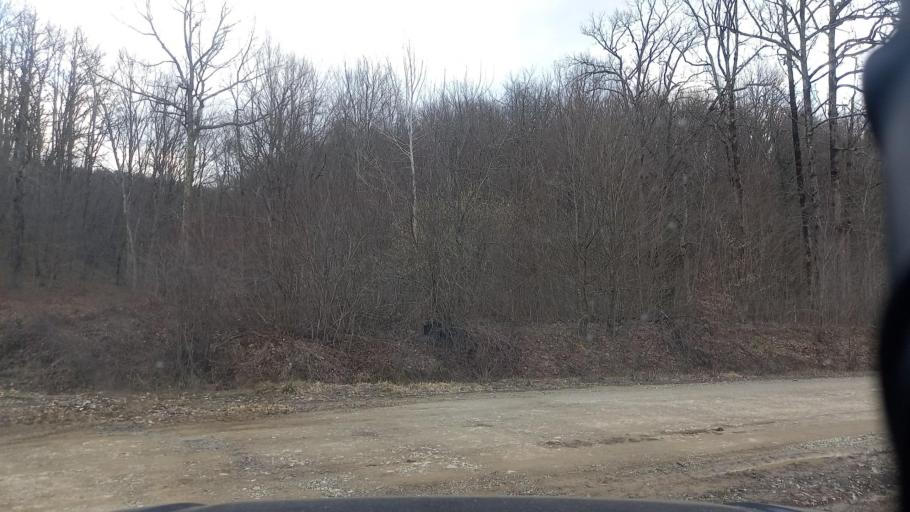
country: RU
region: Krasnodarskiy
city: Lermontovo
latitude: 44.4769
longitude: 38.8047
